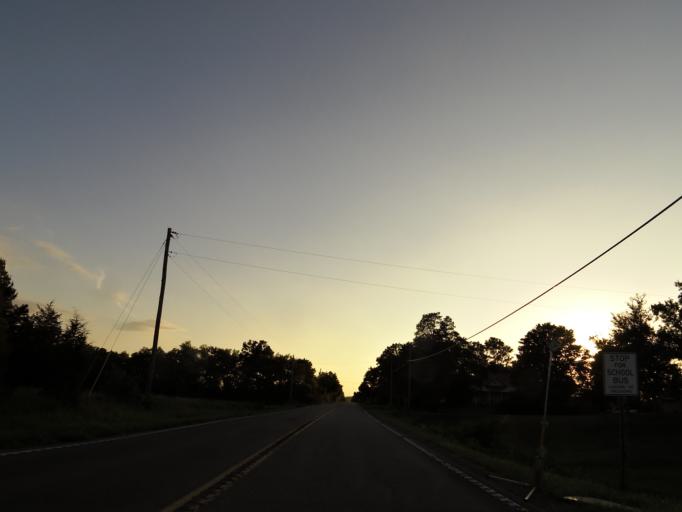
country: US
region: Tennessee
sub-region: Jefferson County
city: New Market
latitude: 36.0236
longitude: -83.5229
